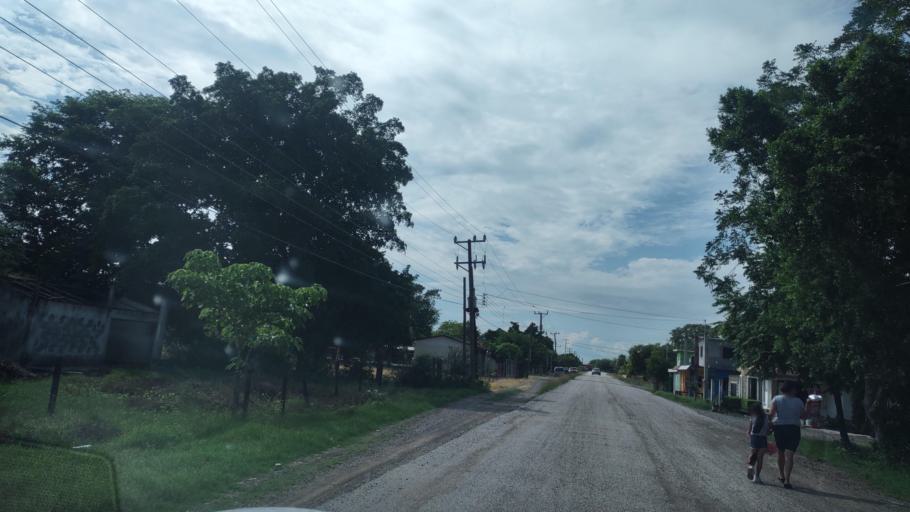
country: MX
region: Veracruz
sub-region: Panuco
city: Oviedo
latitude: 22.0028
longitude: -98.4584
